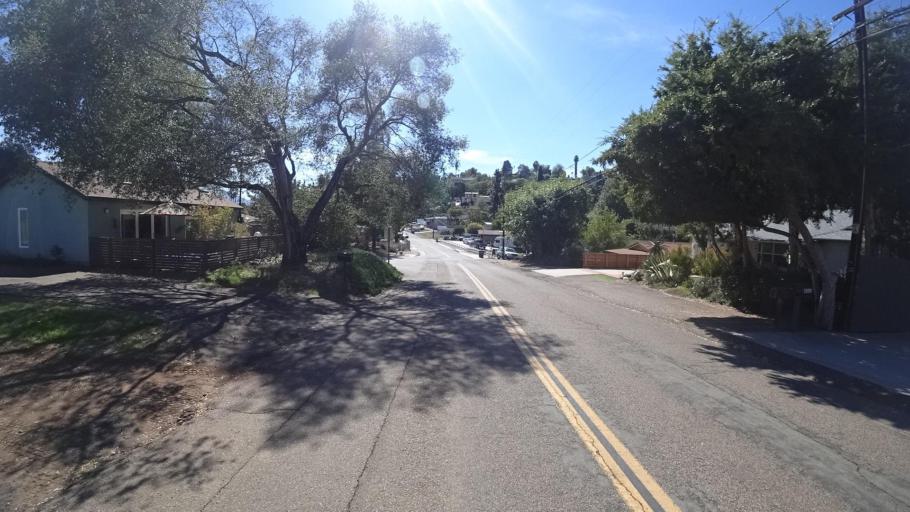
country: US
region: California
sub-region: San Diego County
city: Casa de Oro-Mount Helix
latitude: 32.7519
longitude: -116.9666
